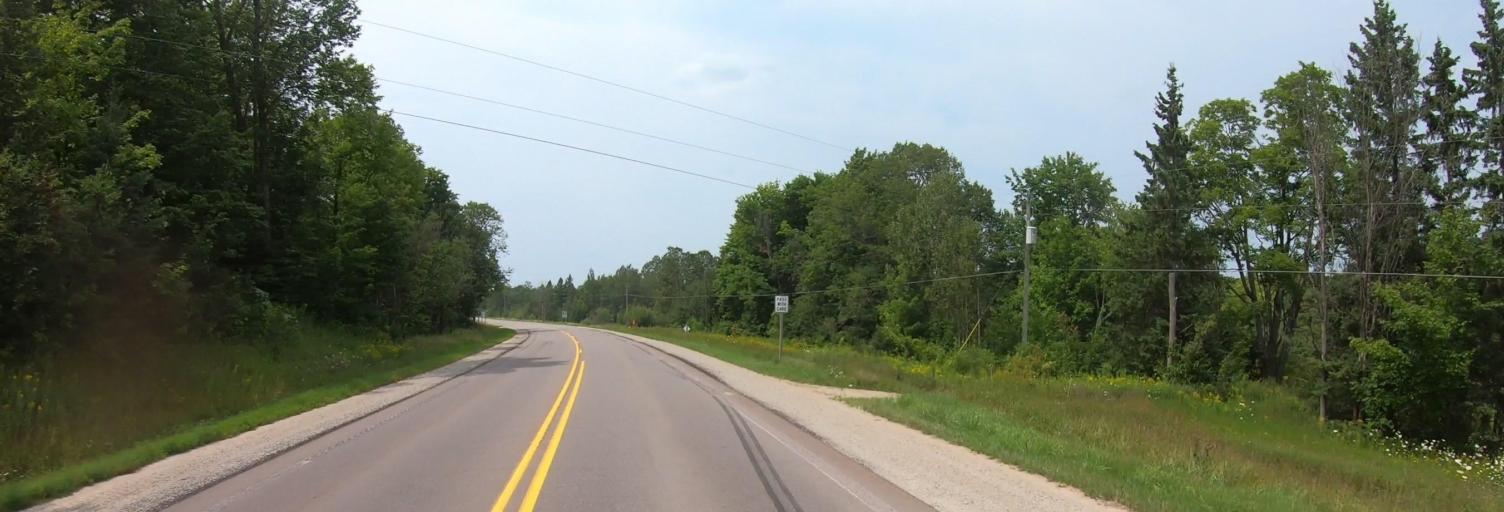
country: US
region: Michigan
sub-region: Alger County
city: Munising
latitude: 46.3545
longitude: -86.9588
